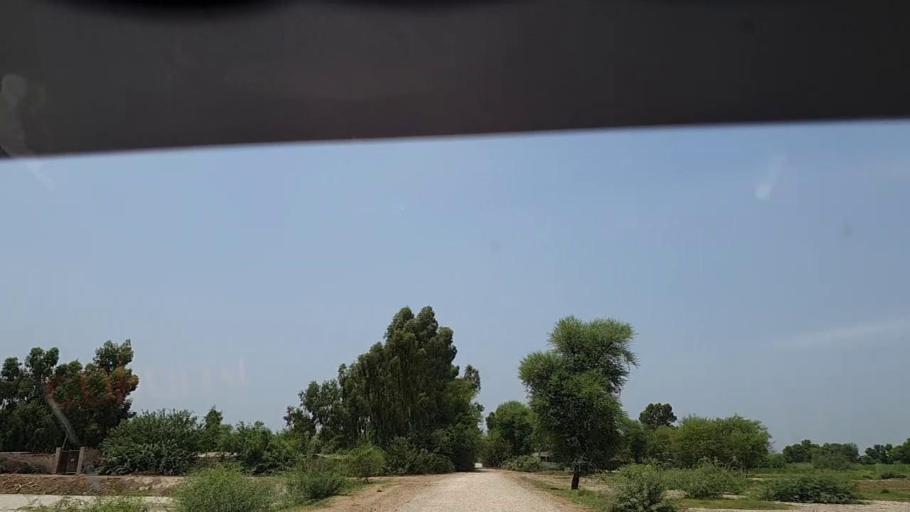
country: PK
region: Sindh
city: Pano Aqil
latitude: 27.9166
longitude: 69.2064
